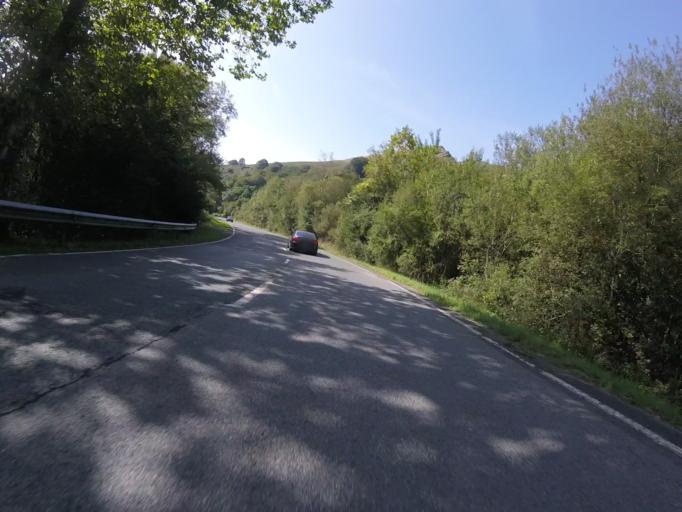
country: ES
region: Navarre
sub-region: Provincia de Navarra
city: Zugarramurdi
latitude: 43.2285
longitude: -1.4986
